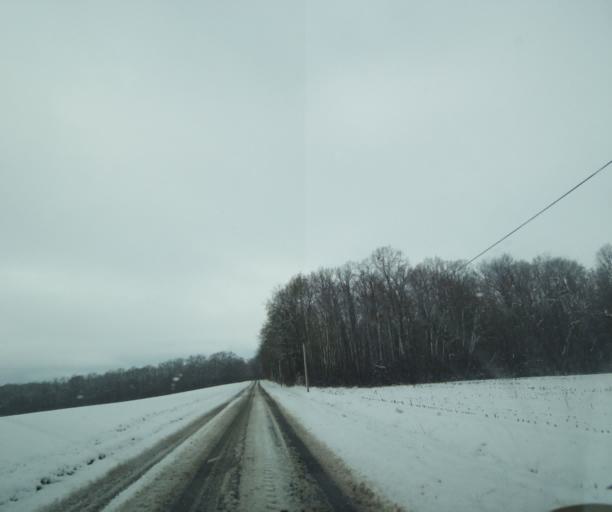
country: FR
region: Champagne-Ardenne
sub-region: Departement de la Haute-Marne
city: Montier-en-Der
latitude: 48.5305
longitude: 4.7398
